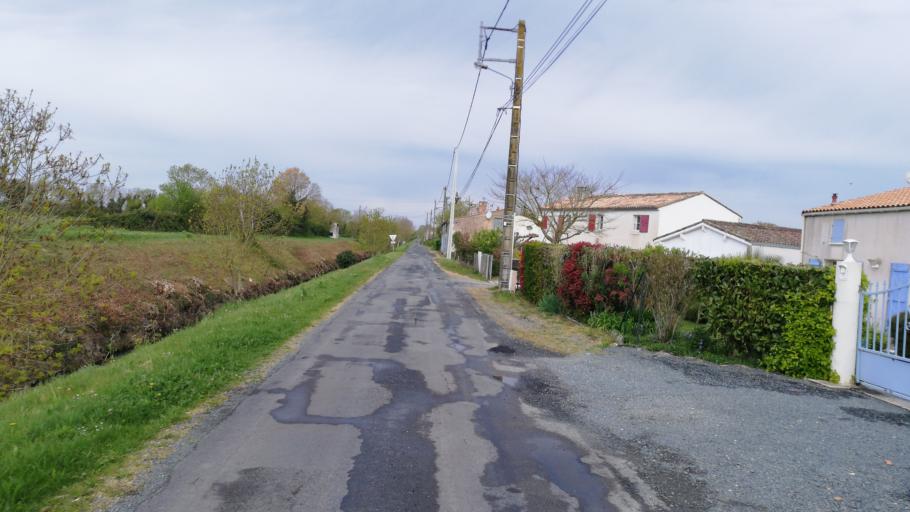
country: FR
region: Pays de la Loire
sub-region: Departement de la Vendee
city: Maillezais
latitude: 46.3270
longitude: -0.7129
